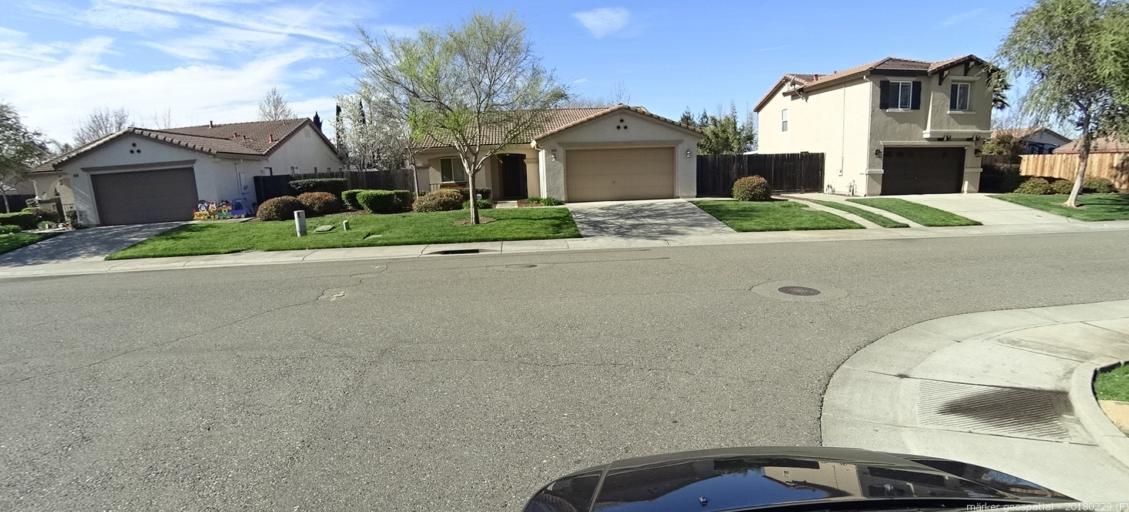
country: US
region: California
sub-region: Sacramento County
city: Rancho Cordova
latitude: 38.5427
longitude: -121.2841
